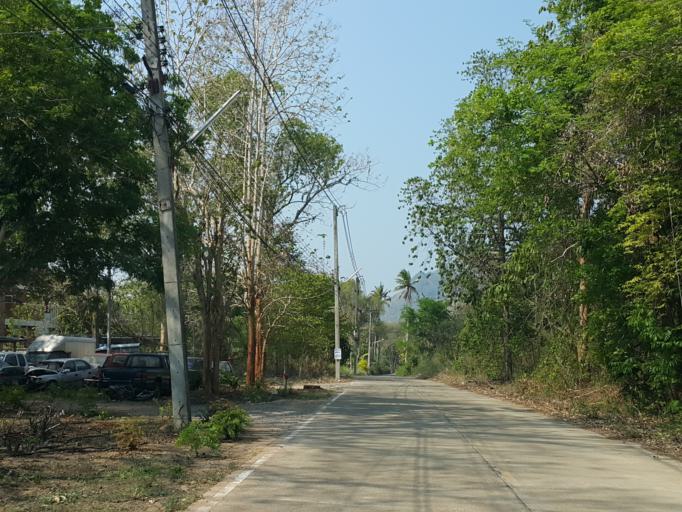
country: TH
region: Kanchanaburi
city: Sai Yok
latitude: 14.1163
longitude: 99.1372
